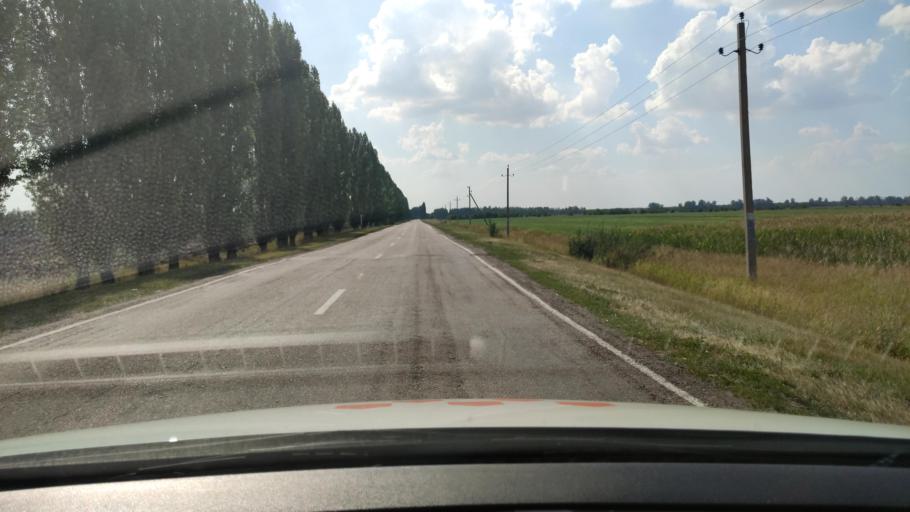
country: RU
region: Voronezj
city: Sadovoye
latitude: 51.7611
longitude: 40.4506
